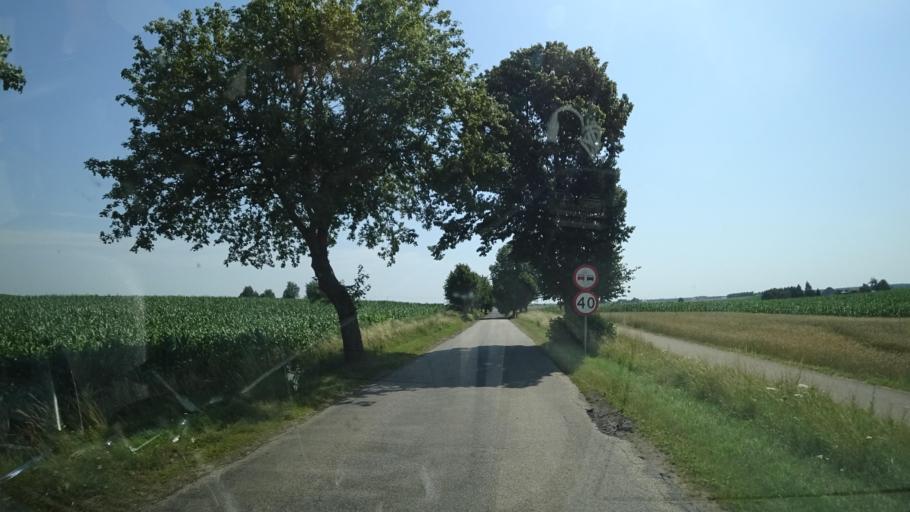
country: PL
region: Pomeranian Voivodeship
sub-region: Powiat chojnicki
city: Brusy
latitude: 53.8774
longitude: 17.6531
